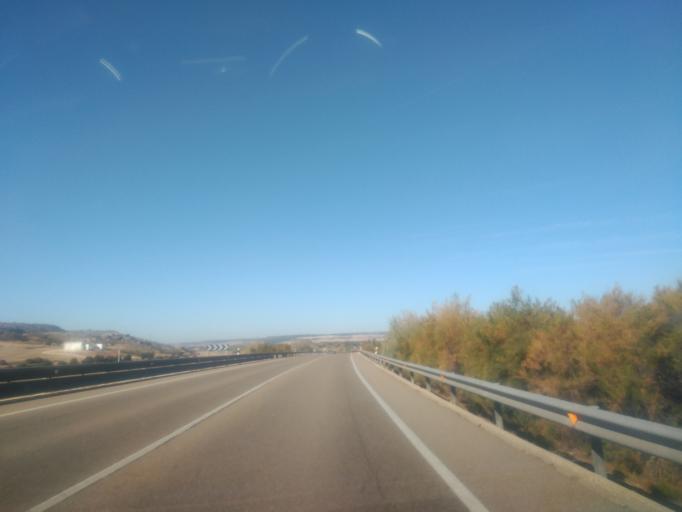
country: ES
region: Castille and Leon
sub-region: Provincia de Valladolid
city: Quintanilla de Arriba
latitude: 41.6180
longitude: -4.2243
